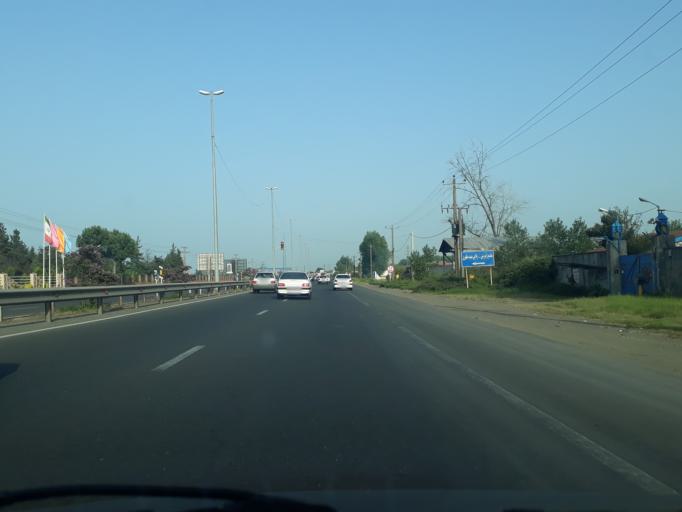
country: IR
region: Gilan
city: Bandar-e Anzali
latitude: 37.4602
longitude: 49.5775
